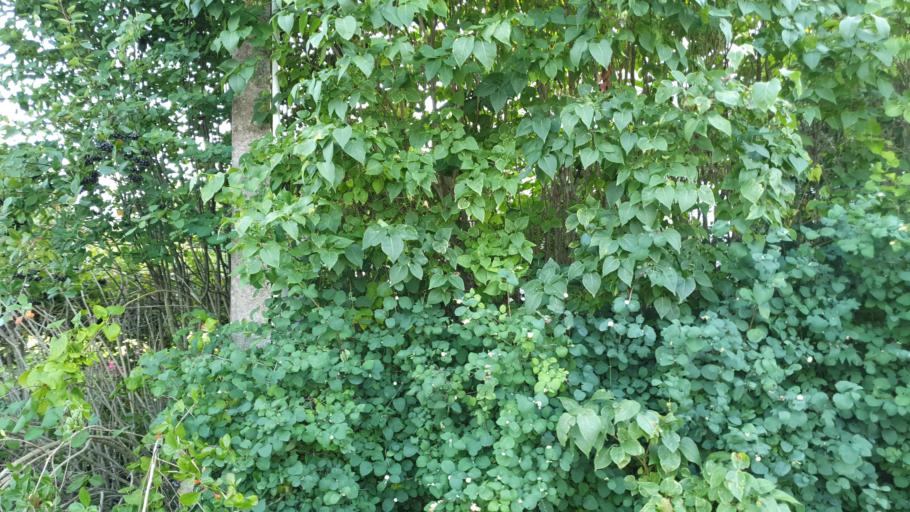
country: RU
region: Leningrad
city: Ivangorod
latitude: 59.4254
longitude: 28.3285
